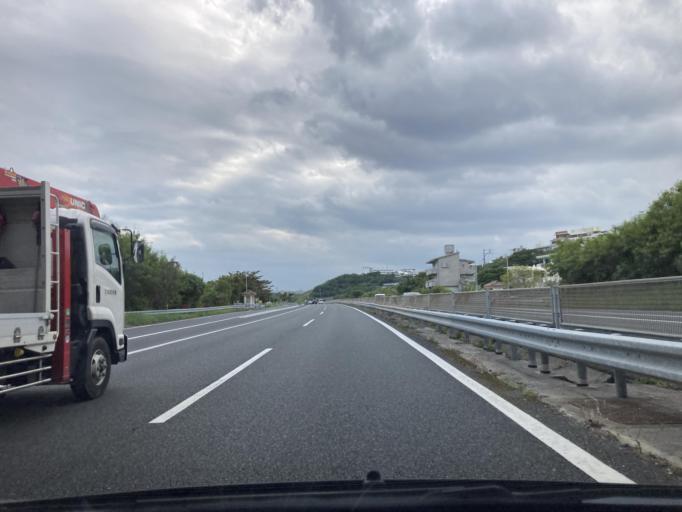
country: JP
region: Okinawa
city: Ginowan
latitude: 26.2402
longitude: 127.7424
